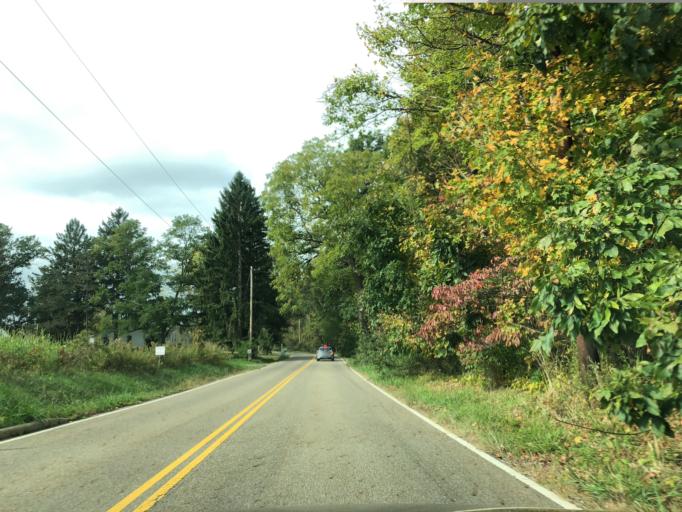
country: US
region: Ohio
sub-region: Summit County
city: Boston Heights
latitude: 41.2632
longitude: -81.5279
